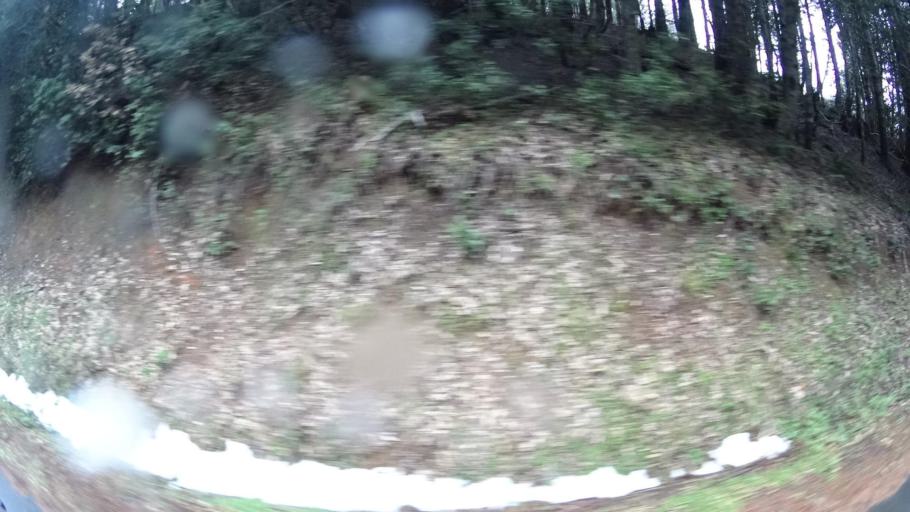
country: US
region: California
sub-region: Humboldt County
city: Willow Creek
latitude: 41.1603
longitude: -123.8178
